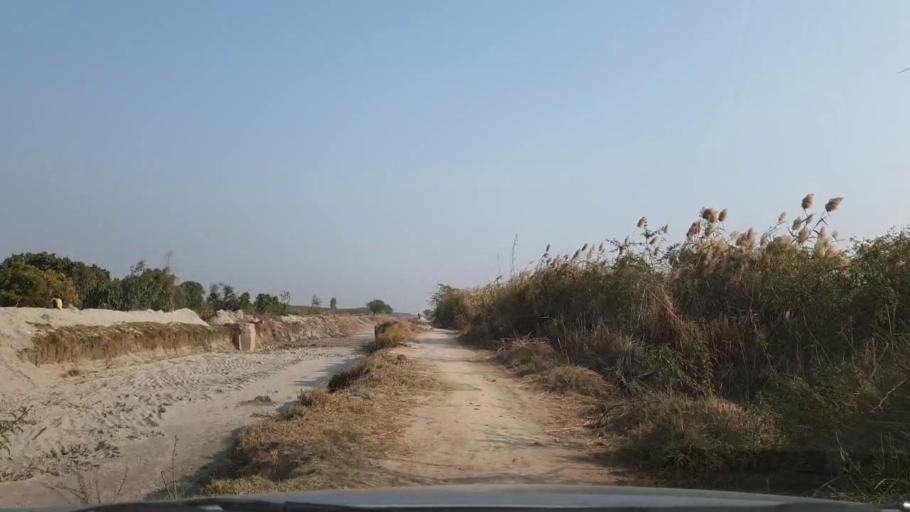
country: PK
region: Sindh
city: Tando Adam
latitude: 25.6481
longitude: 68.5961
